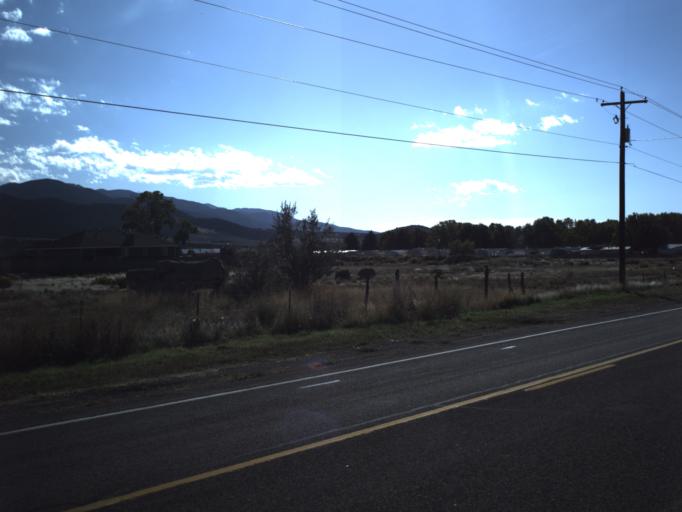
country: US
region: Utah
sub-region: Iron County
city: Parowan
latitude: 37.8386
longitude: -112.8553
